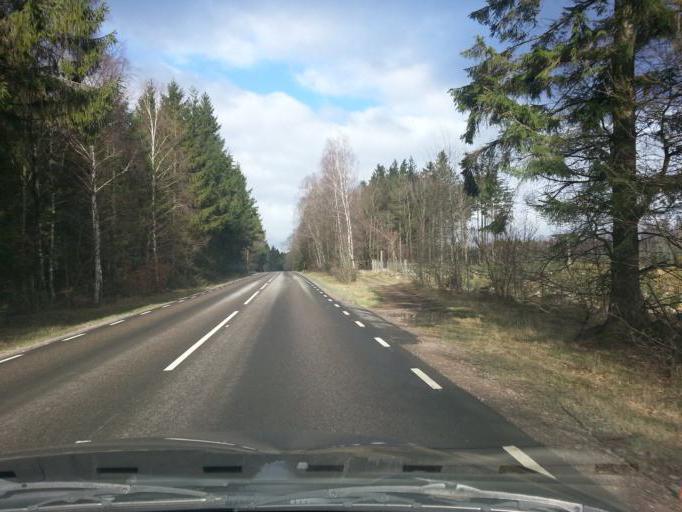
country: SE
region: Skane
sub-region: Astorps Kommun
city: Astorp
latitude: 56.1152
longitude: 12.9879
